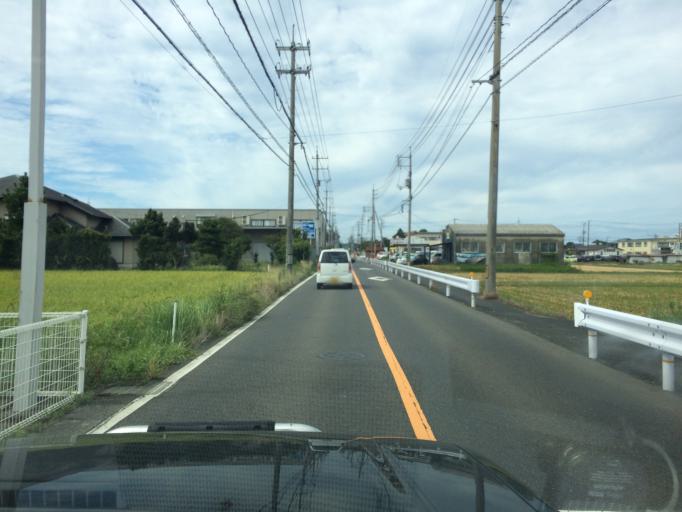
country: JP
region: Tottori
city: Tottori
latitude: 35.5015
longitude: 134.1953
